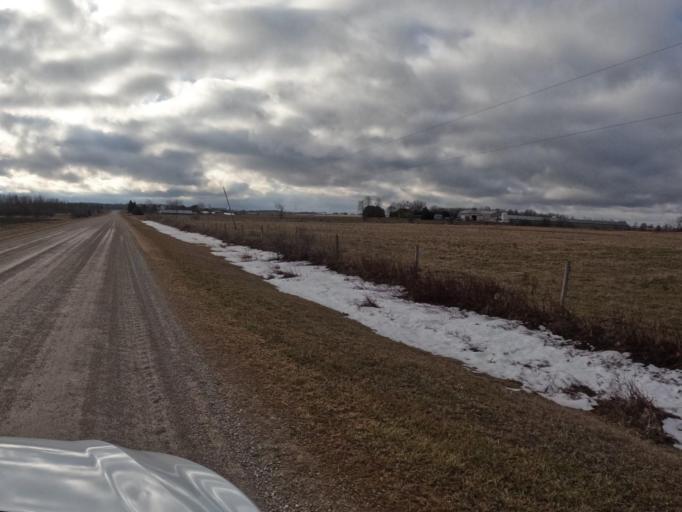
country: CA
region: Ontario
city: Shelburne
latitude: 43.8762
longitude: -80.3569
